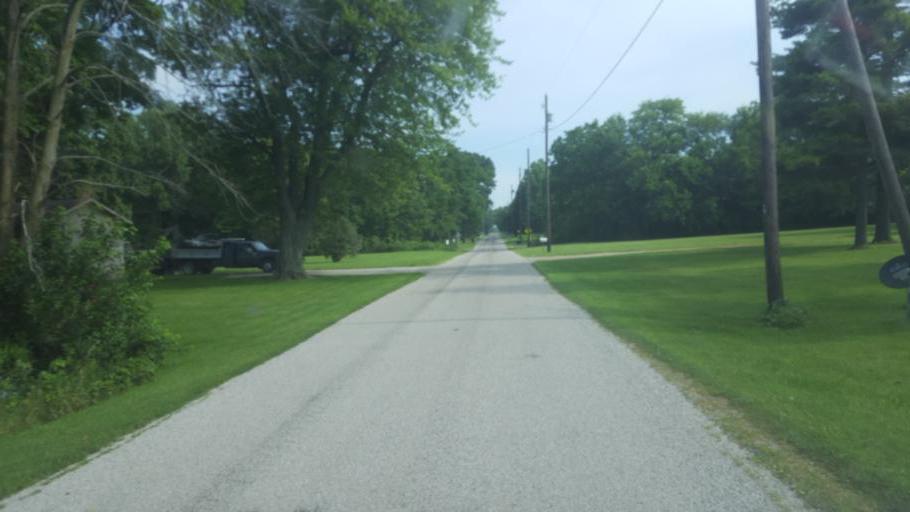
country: US
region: Ohio
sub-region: Marion County
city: Marion
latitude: 40.5970
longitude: -83.2554
